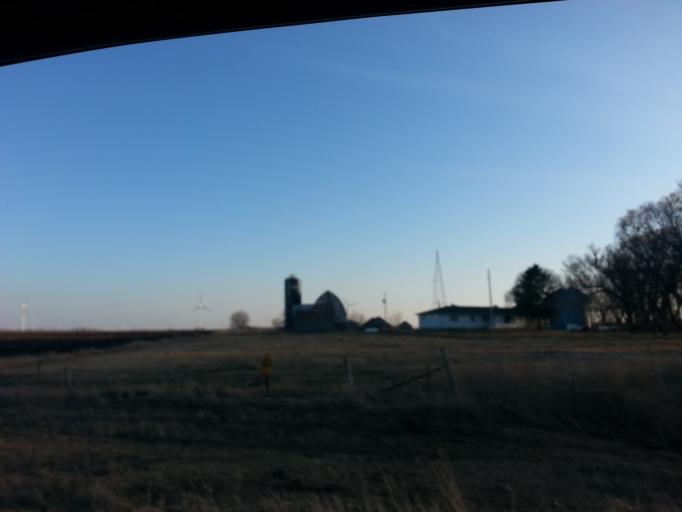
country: US
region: Iowa
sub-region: Worth County
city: Northwood
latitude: 43.4388
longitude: -93.1128
